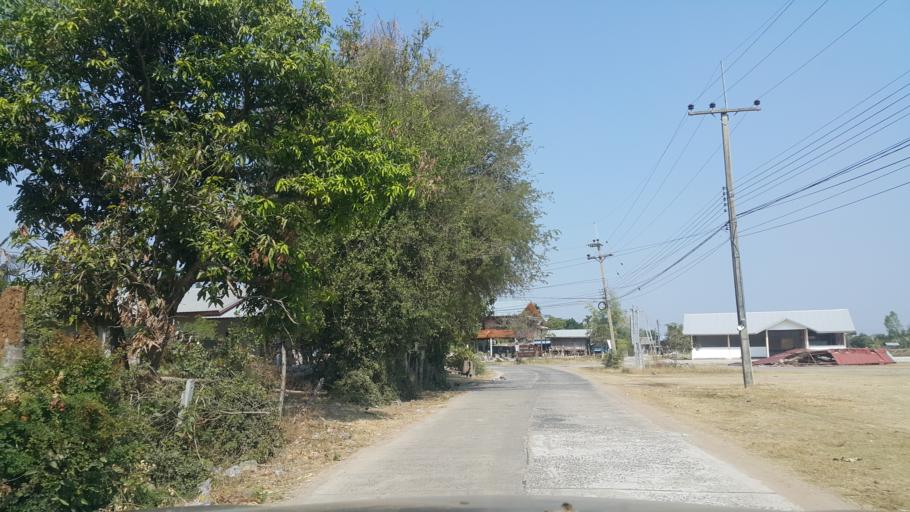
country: TH
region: Buriram
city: Satuek
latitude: 15.1365
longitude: 103.3451
